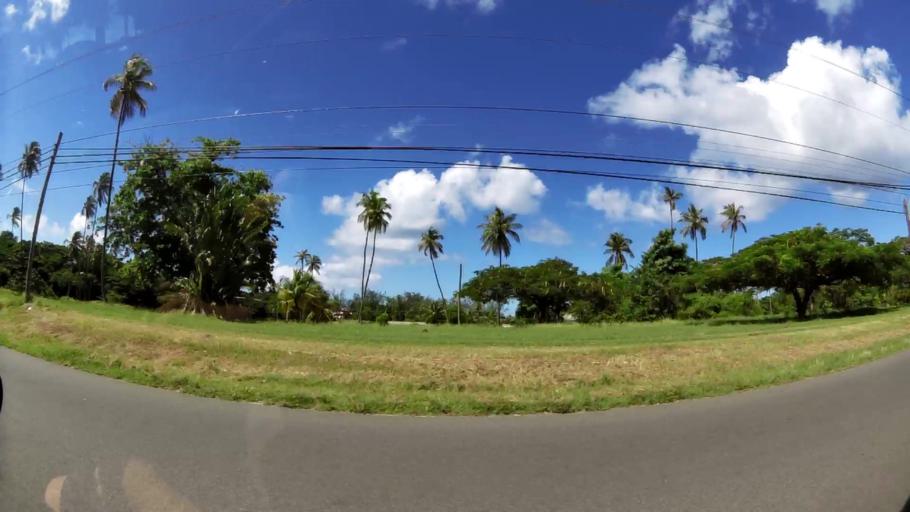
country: TT
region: Tobago
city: Scarborough
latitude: 11.1832
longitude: -60.7996
